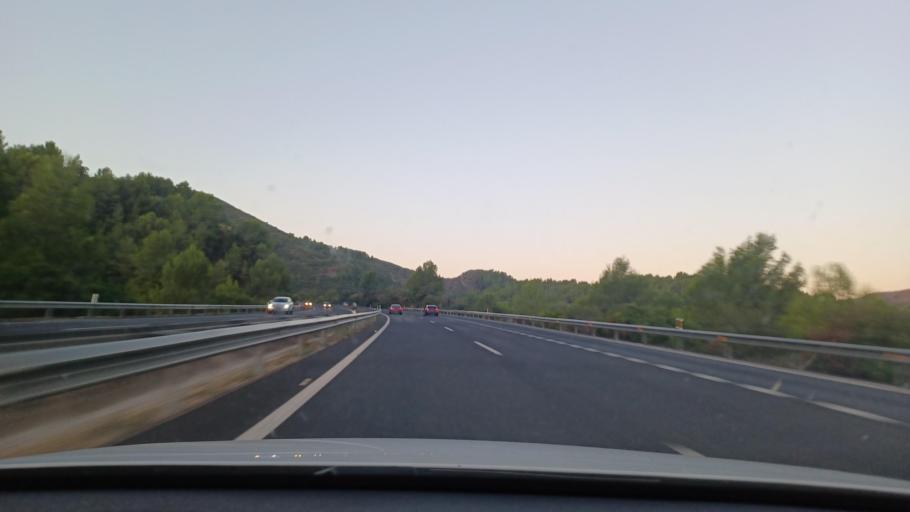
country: ES
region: Valencia
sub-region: Provincia de Alicante
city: Gata de Gorgos
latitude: 38.7618
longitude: 0.0556
